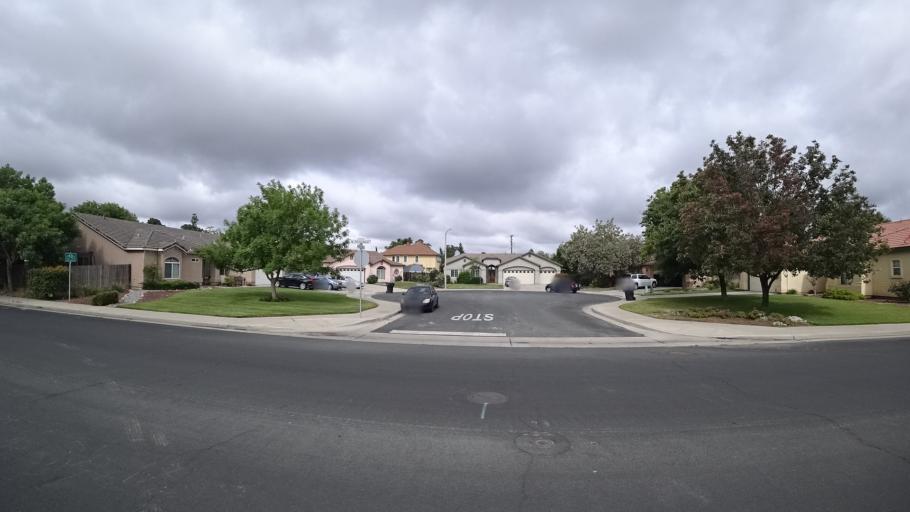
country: US
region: California
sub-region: Kings County
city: Hanford
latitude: 36.3432
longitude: -119.6697
